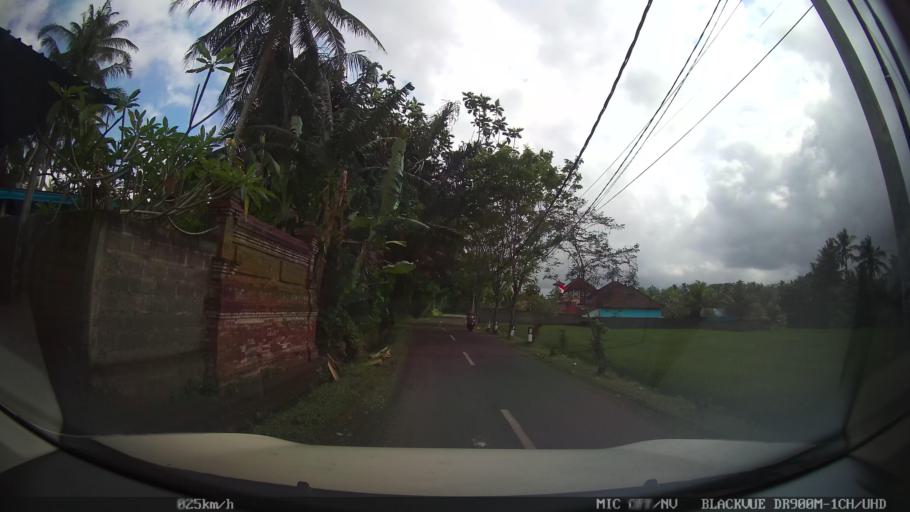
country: ID
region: Bali
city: Banjar Bucu
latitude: -8.5735
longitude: 115.2037
